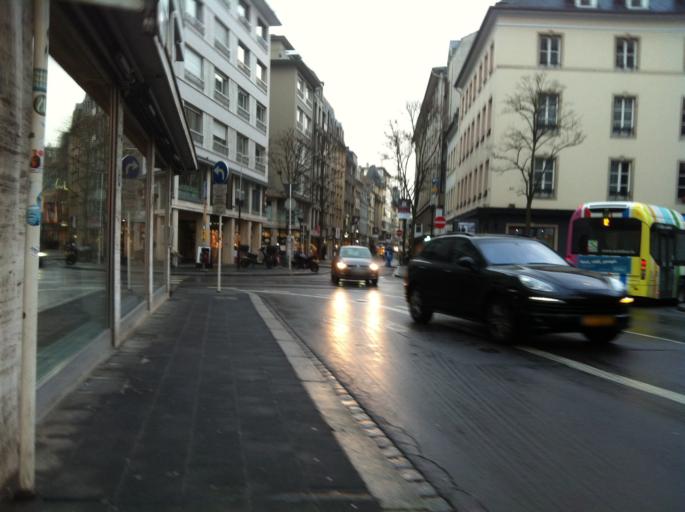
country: LU
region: Luxembourg
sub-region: Canton de Luxembourg
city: Luxembourg
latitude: 49.6135
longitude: 6.1280
